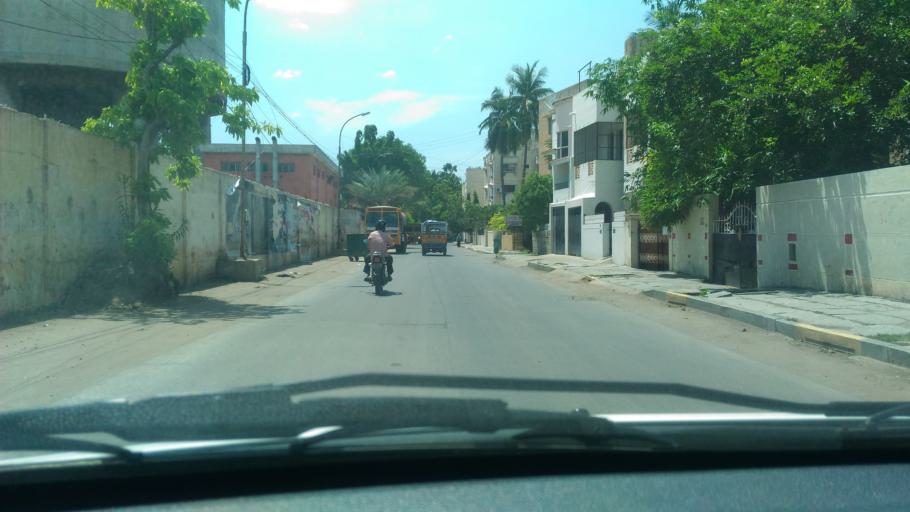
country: IN
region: Tamil Nadu
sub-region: Chennai
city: Chetput
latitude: 13.0515
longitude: 80.2441
